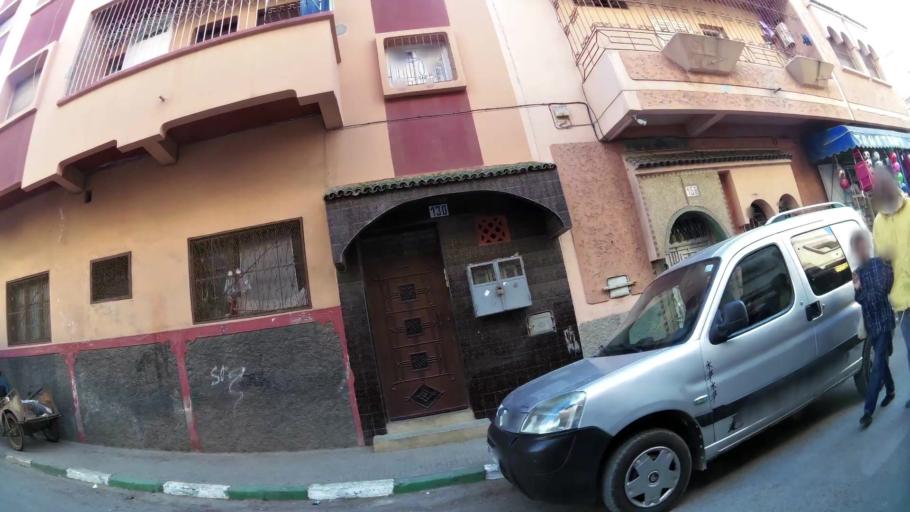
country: MA
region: Rabat-Sale-Zemmour-Zaer
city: Sale
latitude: 34.0547
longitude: -6.7920
